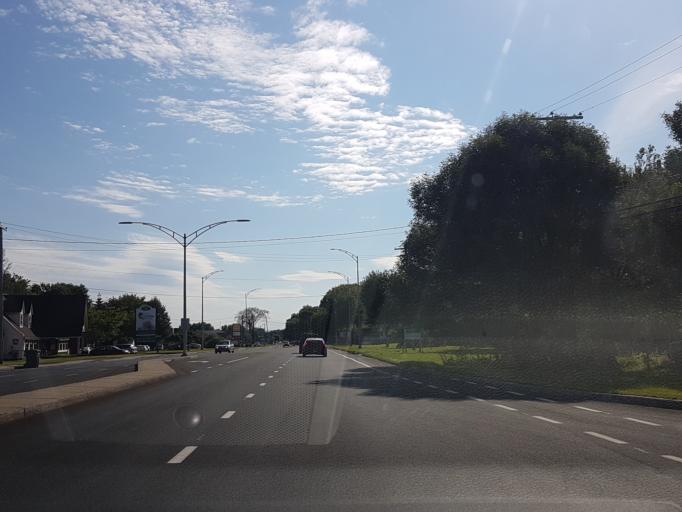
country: CA
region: Quebec
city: Sainte-Catherine
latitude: 46.3129
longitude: -72.5763
